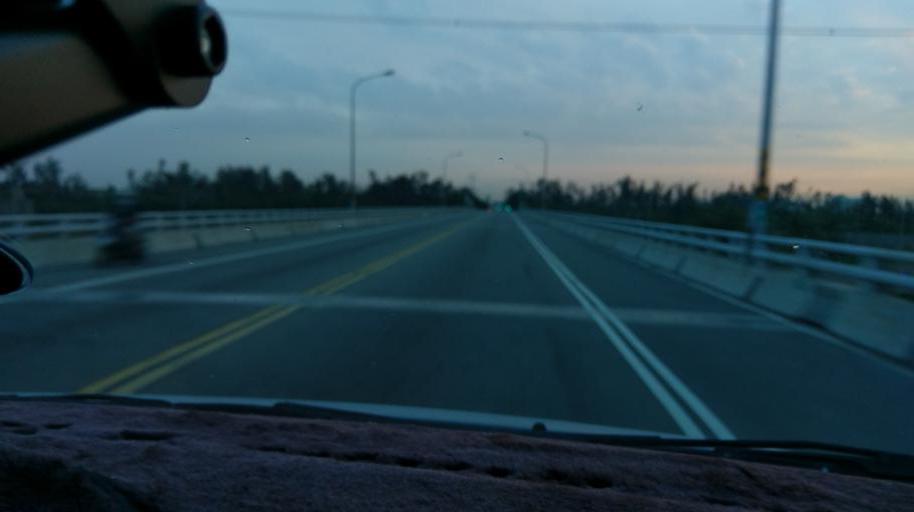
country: TW
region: Taiwan
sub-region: Changhua
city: Chang-hua
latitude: 24.1829
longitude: 120.5032
